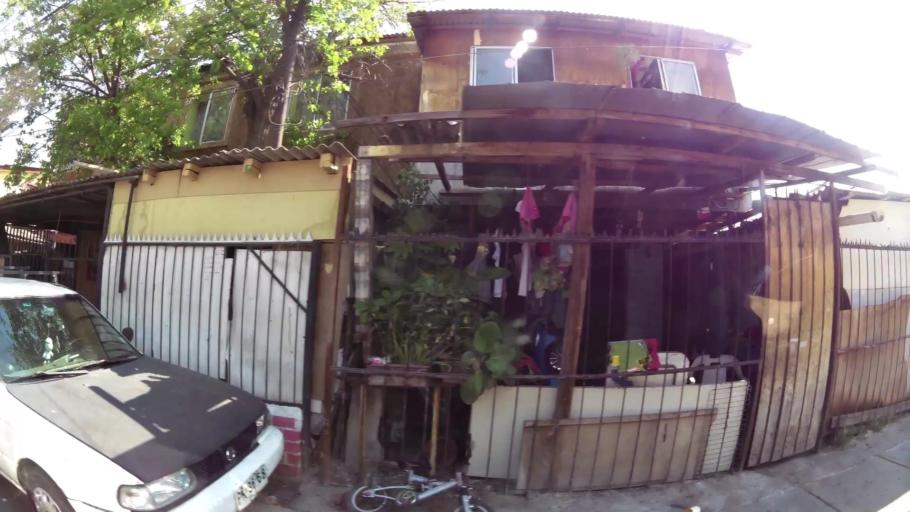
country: CL
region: Santiago Metropolitan
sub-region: Provincia de Santiago
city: La Pintana
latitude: -33.5449
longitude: -70.6030
